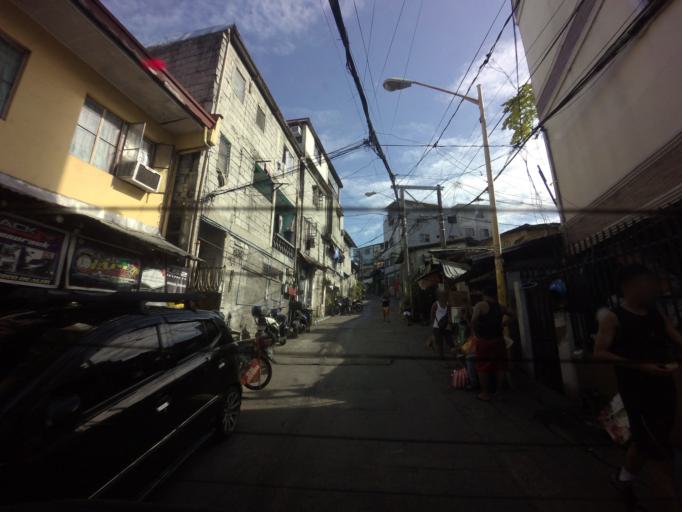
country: PH
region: Metro Manila
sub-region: Mandaluyong
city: Mandaluyong City
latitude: 14.5647
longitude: 121.0487
